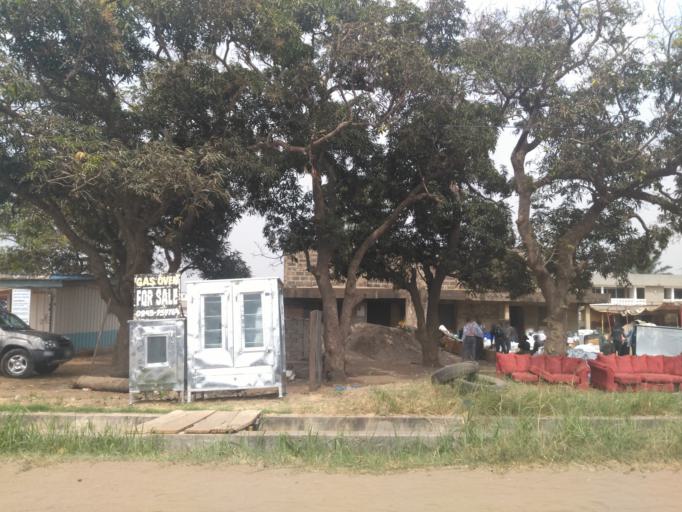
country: GH
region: Greater Accra
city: Nungua
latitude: 5.5962
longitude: -0.0850
